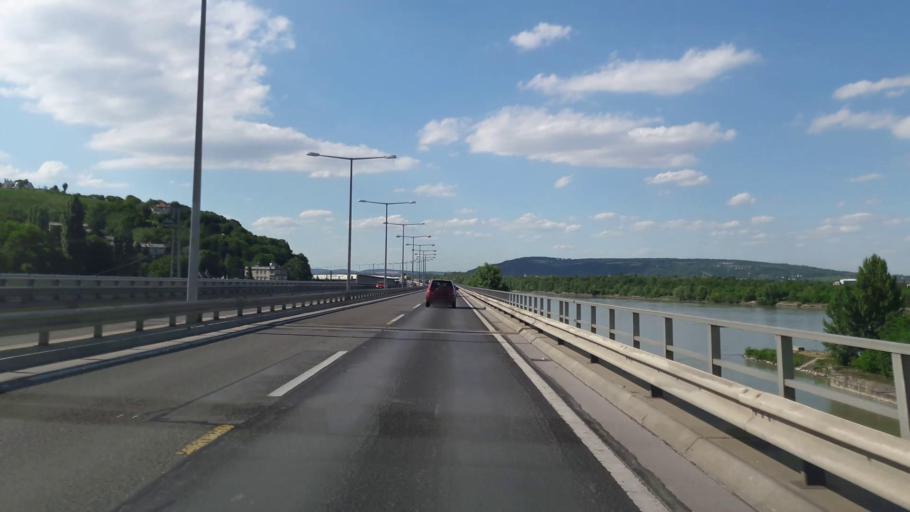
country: AT
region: Lower Austria
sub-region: Politischer Bezirk Korneuburg
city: Langenzersdorf
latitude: 48.2598
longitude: 16.3691
